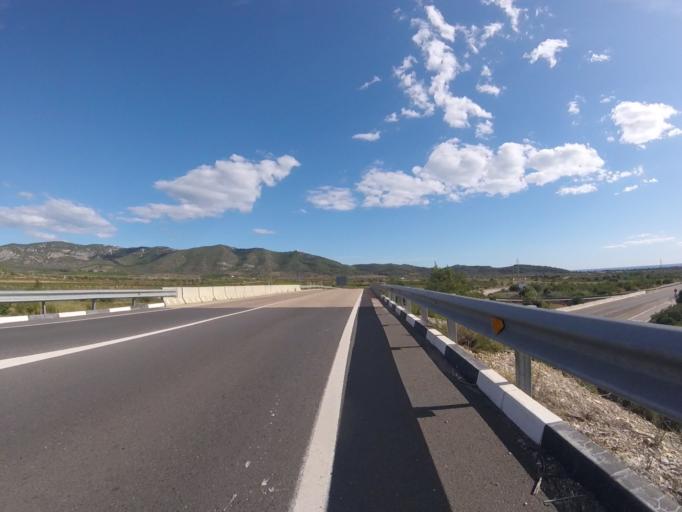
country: ES
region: Valencia
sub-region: Provincia de Castello
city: Alcala de Xivert
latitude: 40.2678
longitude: 0.2403
